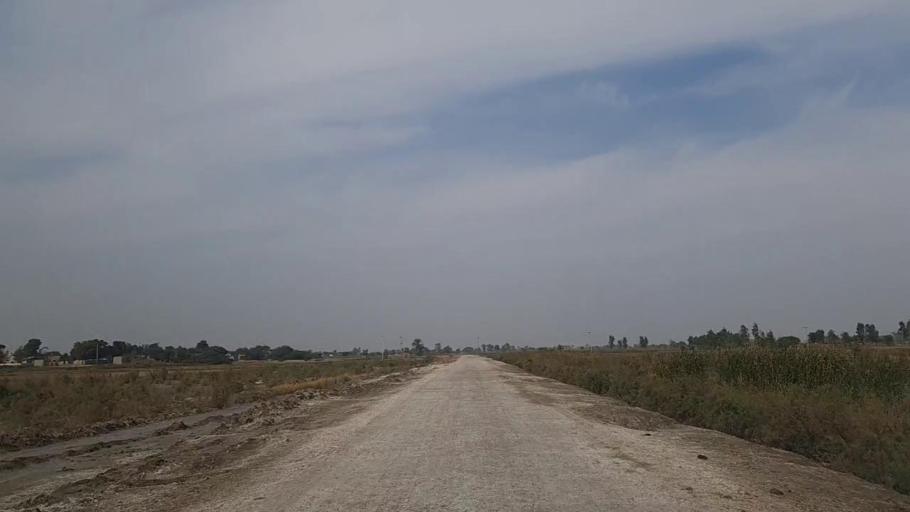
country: PK
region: Sindh
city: Daur
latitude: 26.4797
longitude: 68.4055
